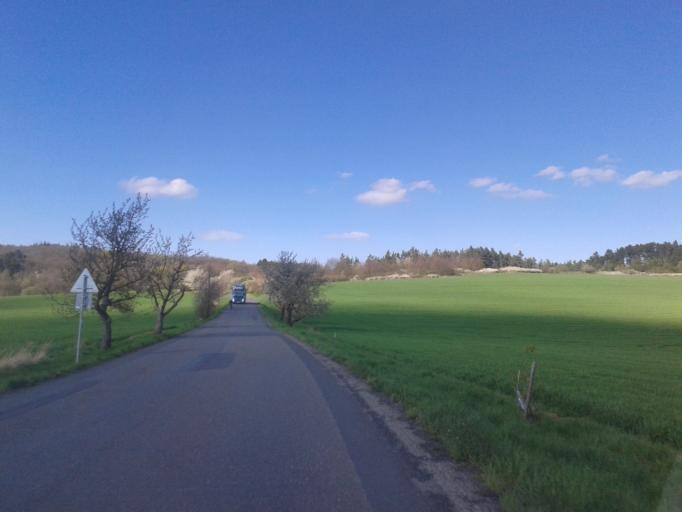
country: CZ
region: Central Bohemia
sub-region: Okres Beroun
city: Beroun
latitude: 49.8967
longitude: 14.0761
